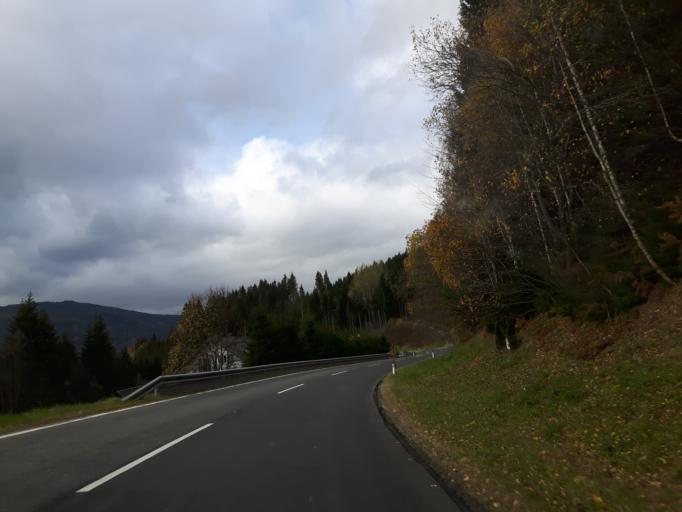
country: AT
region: Styria
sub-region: Politischer Bezirk Deutschlandsberg
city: Soboth
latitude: 46.7050
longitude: 15.1043
